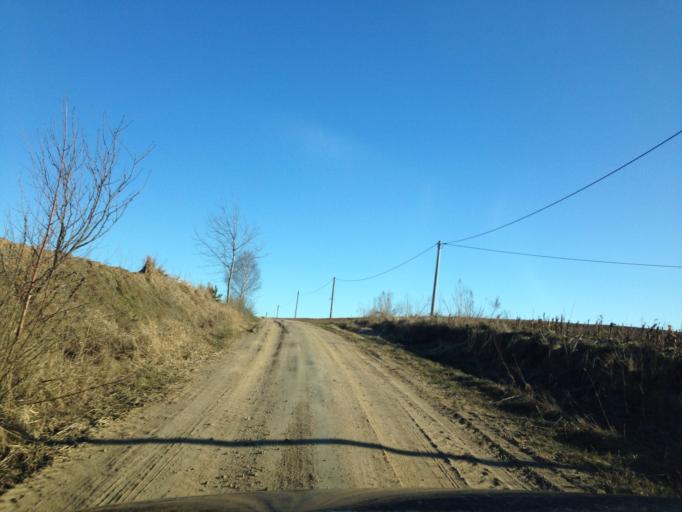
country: PL
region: Kujawsko-Pomorskie
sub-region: Powiat brodnicki
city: Brzozie
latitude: 53.3165
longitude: 19.6576
